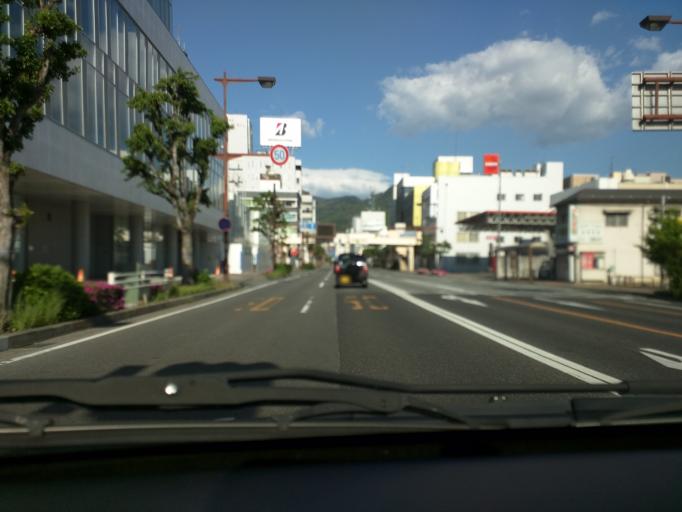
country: JP
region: Nagano
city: Nagano-shi
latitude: 36.6489
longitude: 138.1954
